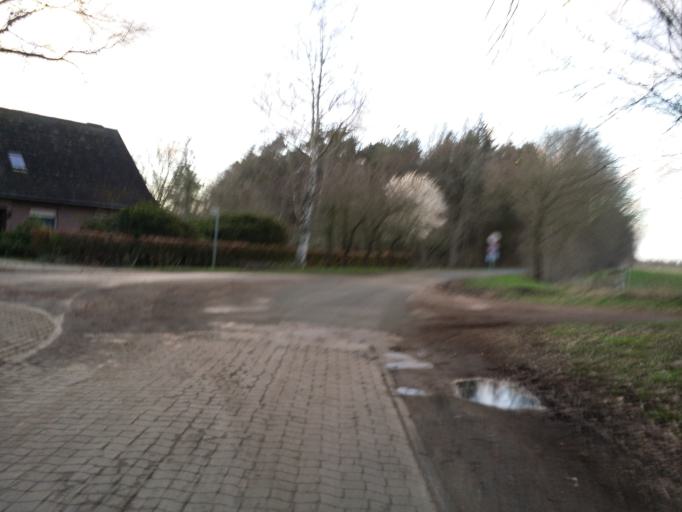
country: DE
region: Lower Saxony
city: Gross Ippener
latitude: 52.9763
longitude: 8.5964
